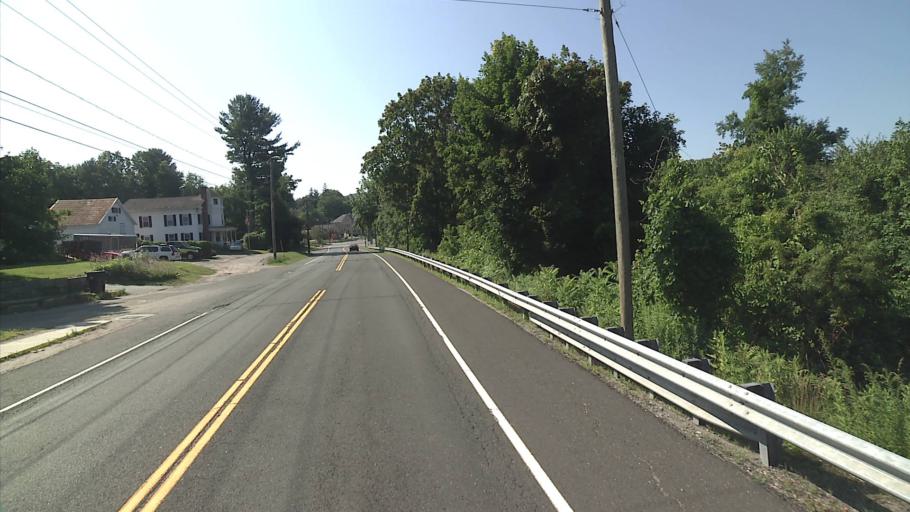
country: US
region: Connecticut
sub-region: Litchfield County
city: Winsted
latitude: 41.9284
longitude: -73.0776
